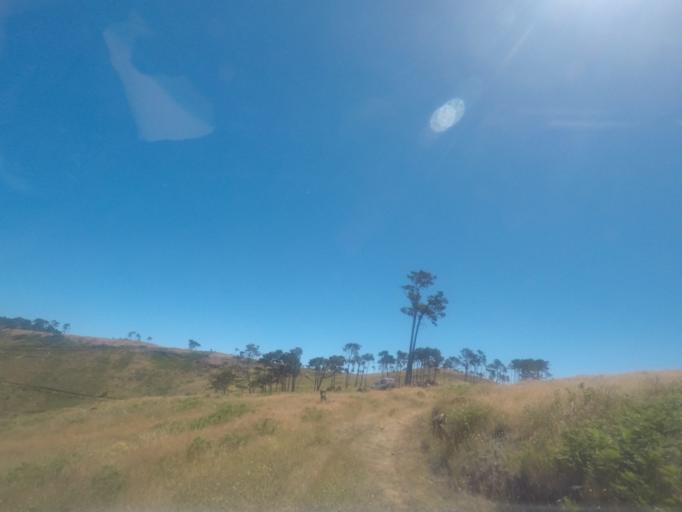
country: PT
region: Madeira
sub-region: Funchal
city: Nossa Senhora do Monte
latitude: 32.7122
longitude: -16.9138
